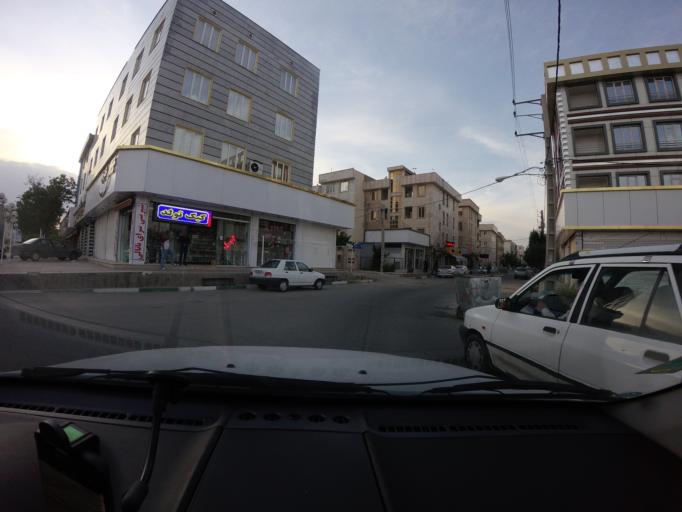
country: IR
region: Tehran
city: Eslamshahr
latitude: 35.5266
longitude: 51.2305
